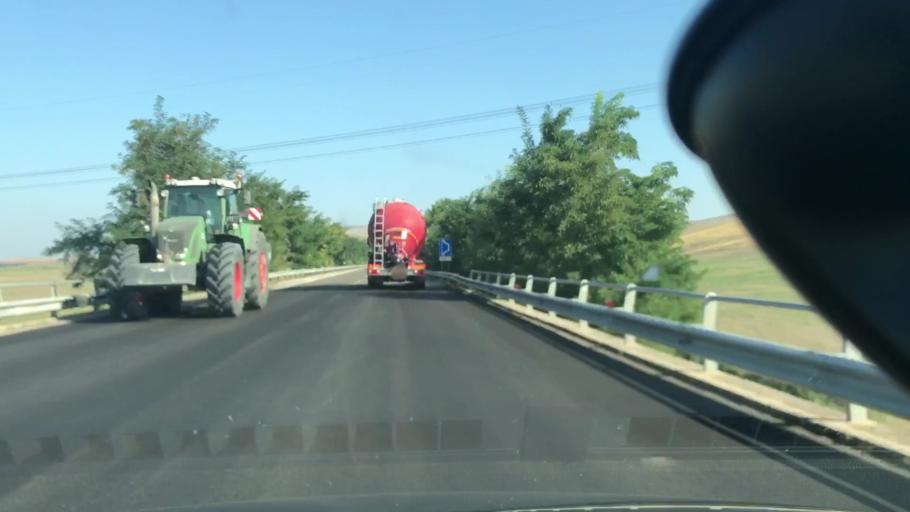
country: IT
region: Basilicate
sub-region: Provincia di Matera
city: Irsina
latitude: 40.7992
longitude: 16.2748
